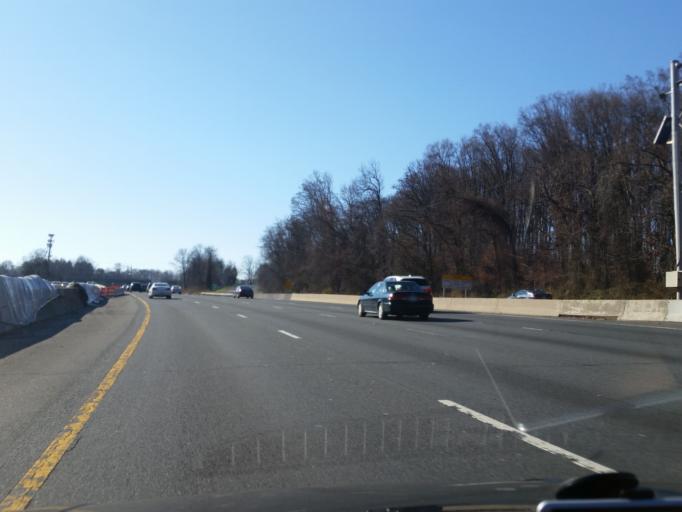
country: US
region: Virginia
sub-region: Fairfax County
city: McLean
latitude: 38.9587
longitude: -77.1921
